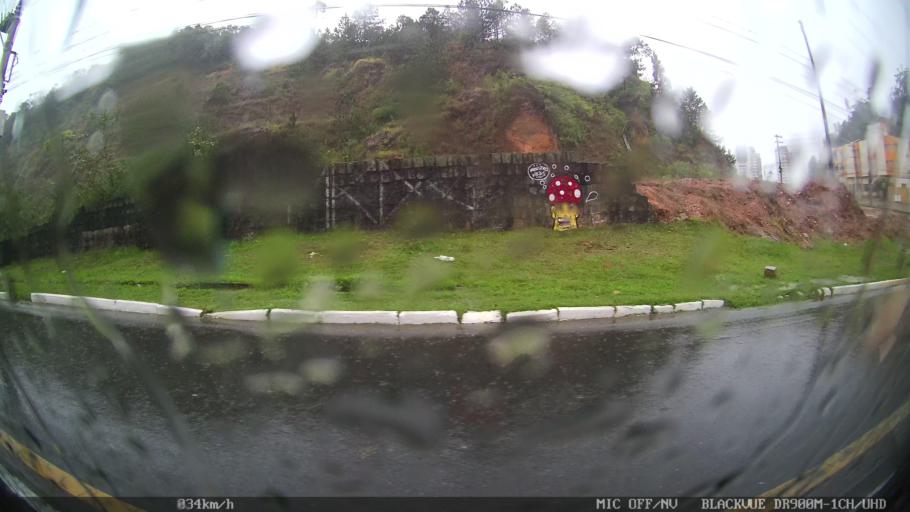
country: BR
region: Santa Catarina
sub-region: Itajai
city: Itajai
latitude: -26.9362
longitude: -48.6414
